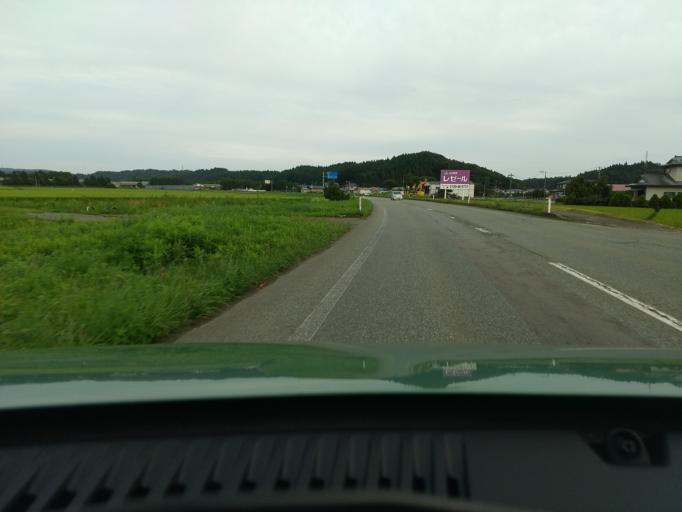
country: JP
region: Akita
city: Akita Shi
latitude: 39.7965
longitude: 140.0958
